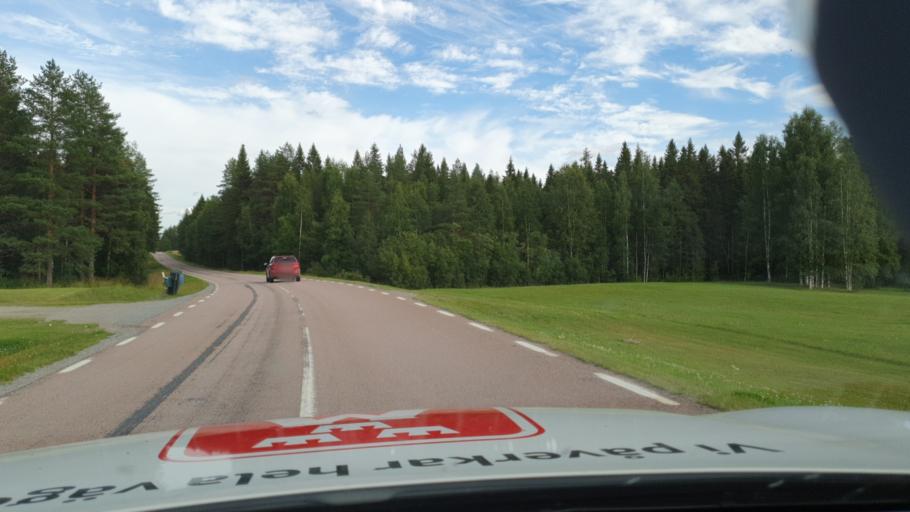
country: SE
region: Jaemtland
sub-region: Stroemsunds Kommun
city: Stroemsund
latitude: 63.6577
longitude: 15.9722
